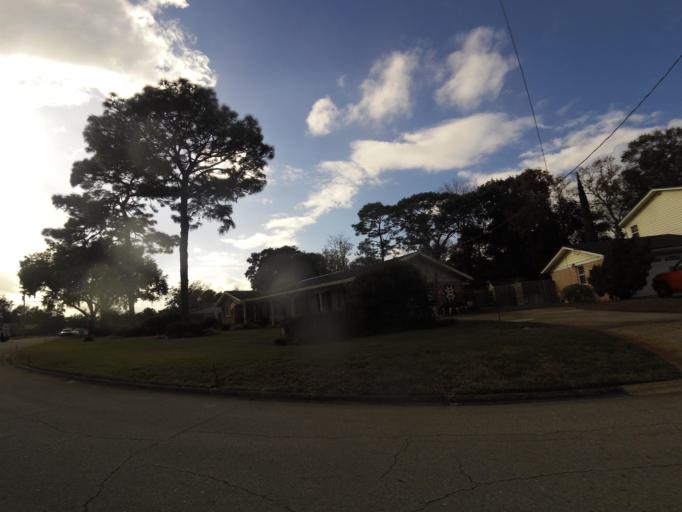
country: US
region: Florida
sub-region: Duval County
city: Jacksonville
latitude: 30.3425
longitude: -81.5793
